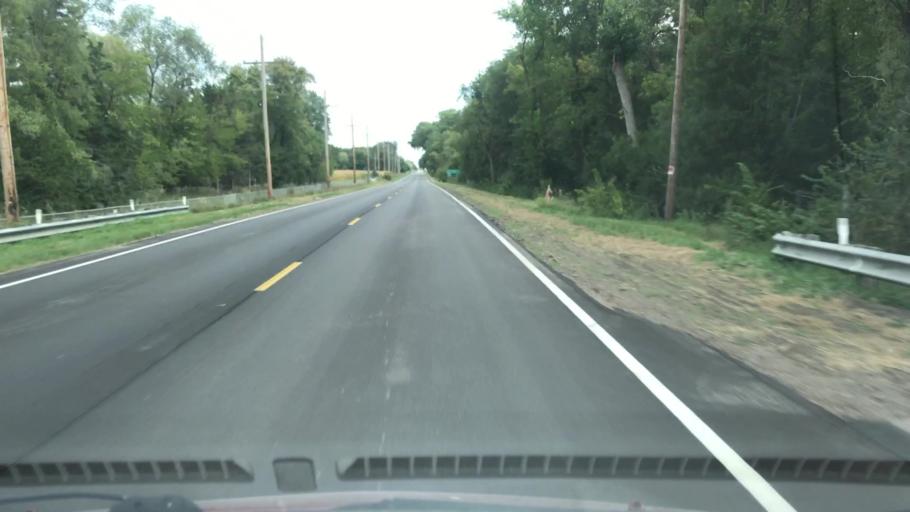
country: US
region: Nebraska
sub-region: Hall County
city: Grand Island
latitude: 40.9237
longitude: -98.3015
